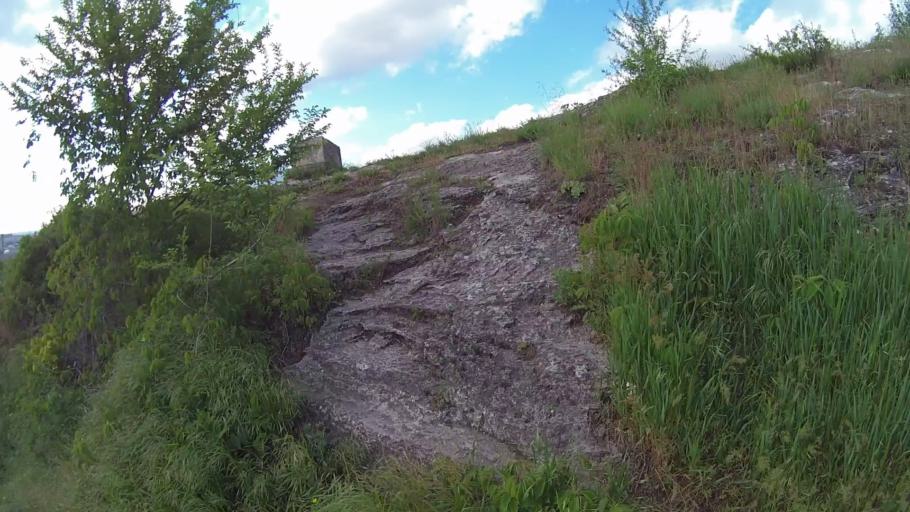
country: RU
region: Stavropol'skiy
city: Goryachevodskiy
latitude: 44.0355
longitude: 43.0829
